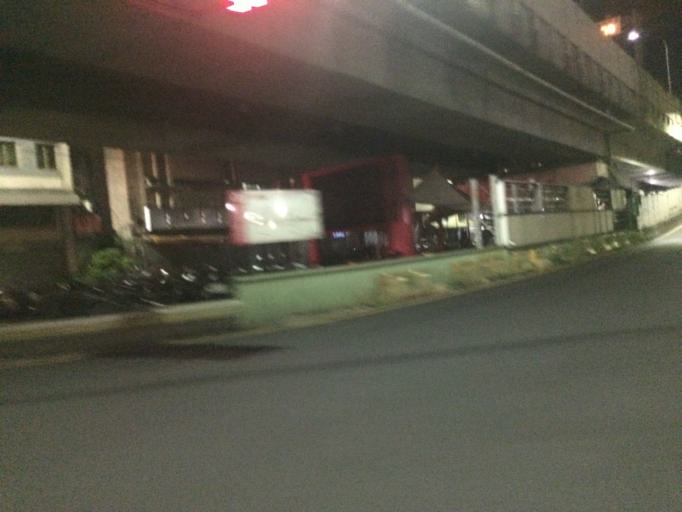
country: TW
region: Taiwan
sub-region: Hsinchu
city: Hsinchu
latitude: 24.8036
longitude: 120.9788
